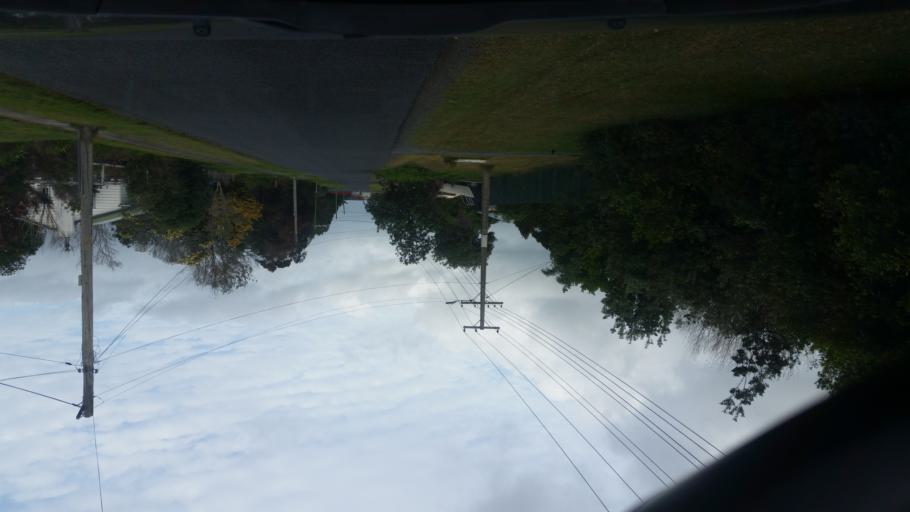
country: NZ
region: Northland
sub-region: Kaipara District
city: Dargaville
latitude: -36.0300
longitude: 173.9167
